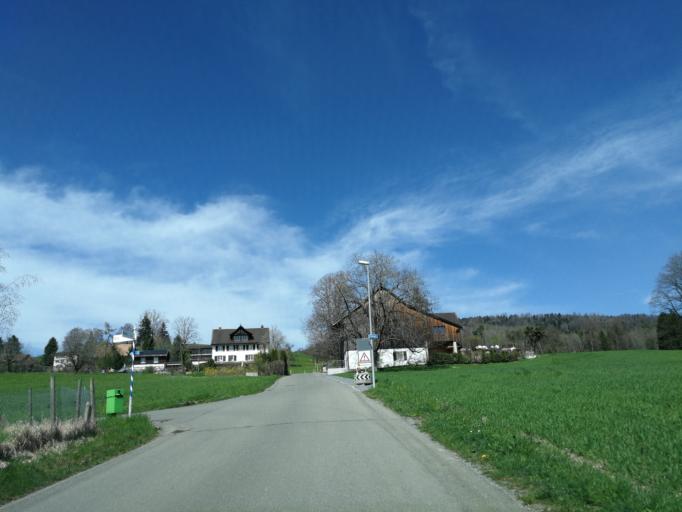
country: CH
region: Zurich
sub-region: Bezirk Meilen
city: Meilen
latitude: 47.2774
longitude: 8.6536
